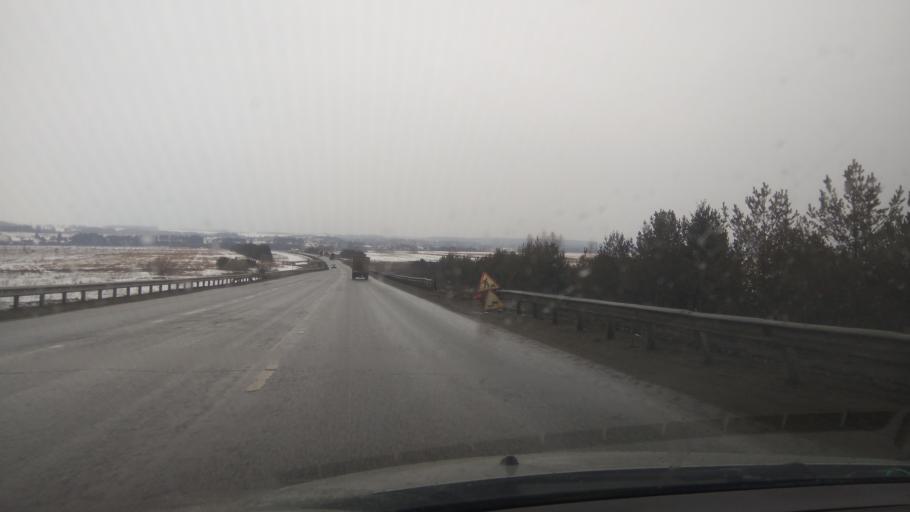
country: RU
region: Perm
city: Kungur
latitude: 57.3578
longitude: 56.9317
